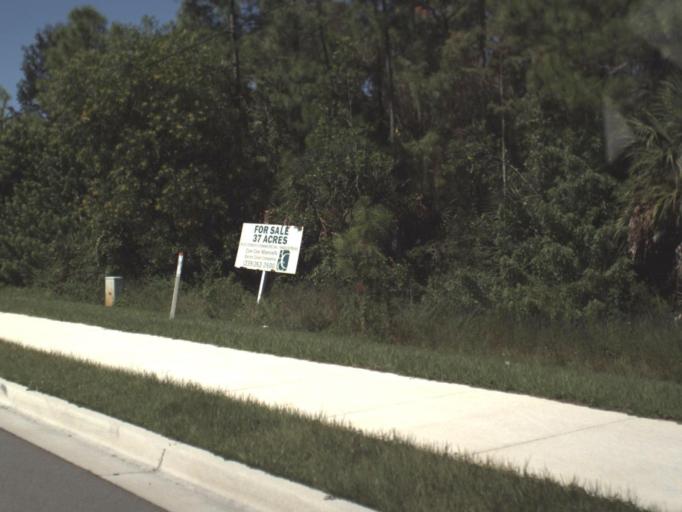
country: US
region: Florida
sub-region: Collier County
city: Golden Gate
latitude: 26.1549
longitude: -81.6923
